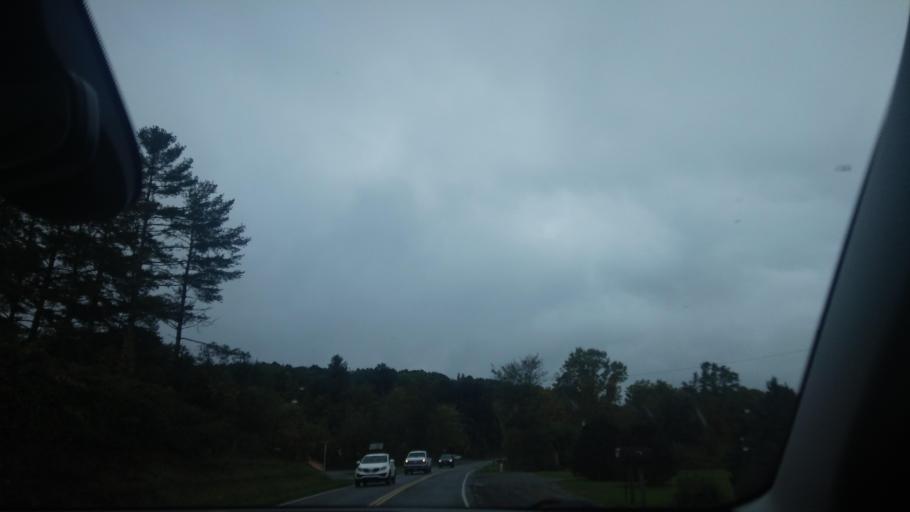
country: US
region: Virginia
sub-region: City of Galax
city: Galax
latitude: 36.6367
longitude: -80.9180
